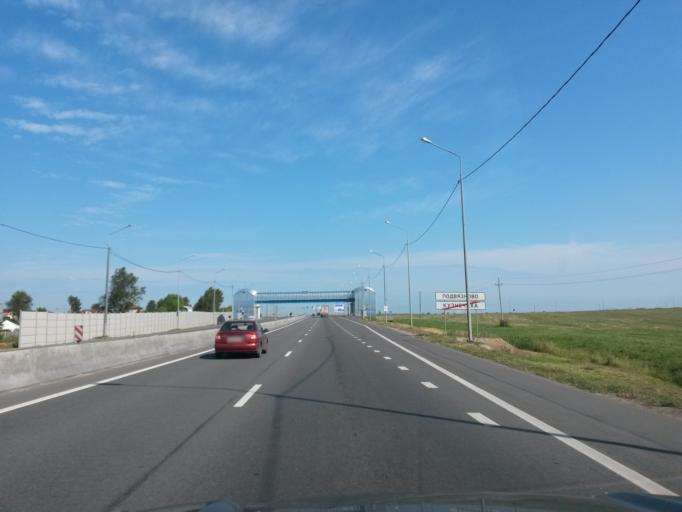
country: RU
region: Jaroslavl
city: Yaroslavl
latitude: 57.7161
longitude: 39.9031
